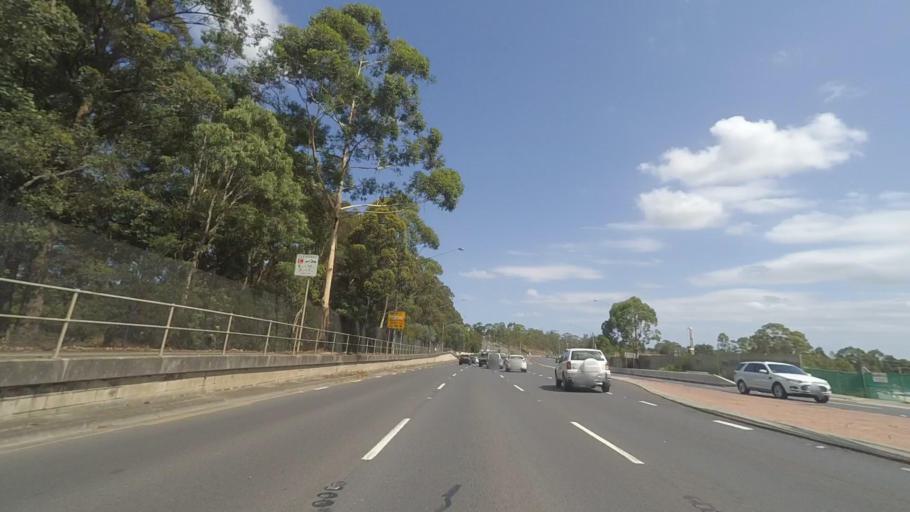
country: AU
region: New South Wales
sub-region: The Hills Shire
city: West Pennant
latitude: -33.7562
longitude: 151.0485
